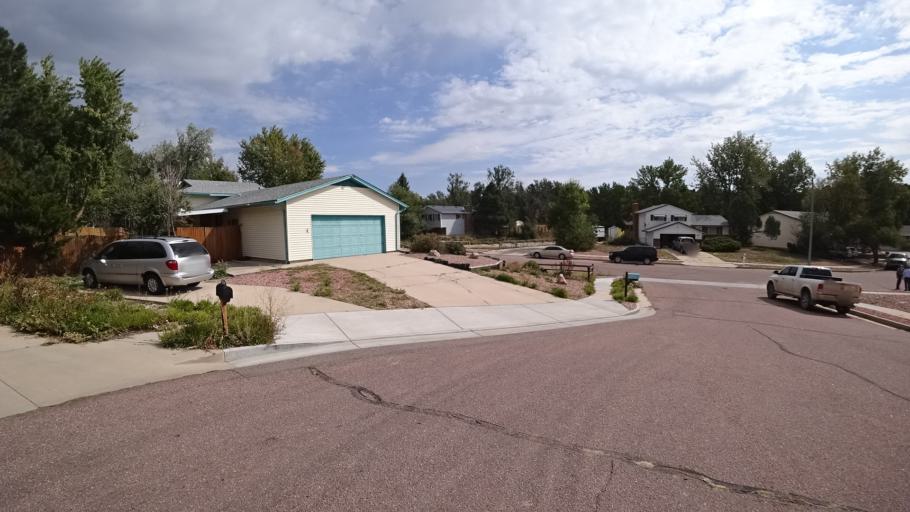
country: US
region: Colorado
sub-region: El Paso County
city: Cimarron Hills
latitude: 38.8584
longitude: -104.7336
